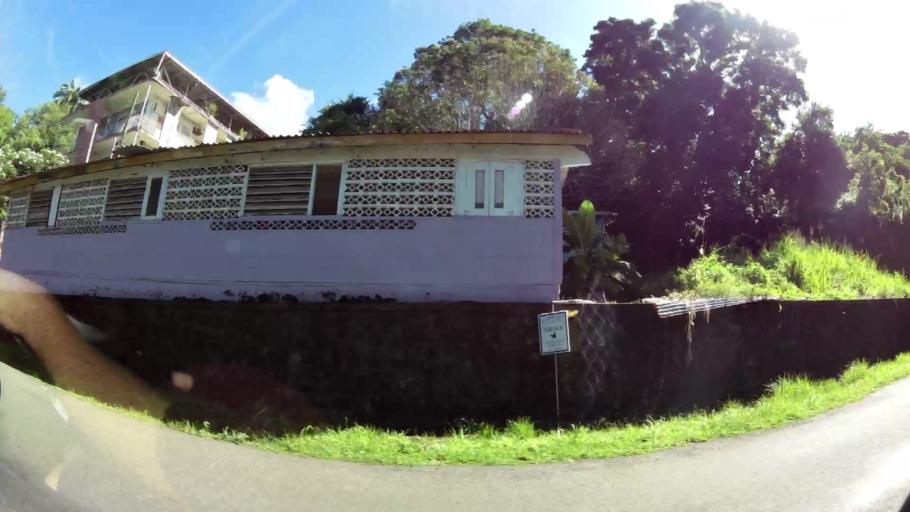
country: TT
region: Tobago
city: Scarborough
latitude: 11.1724
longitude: -60.7225
